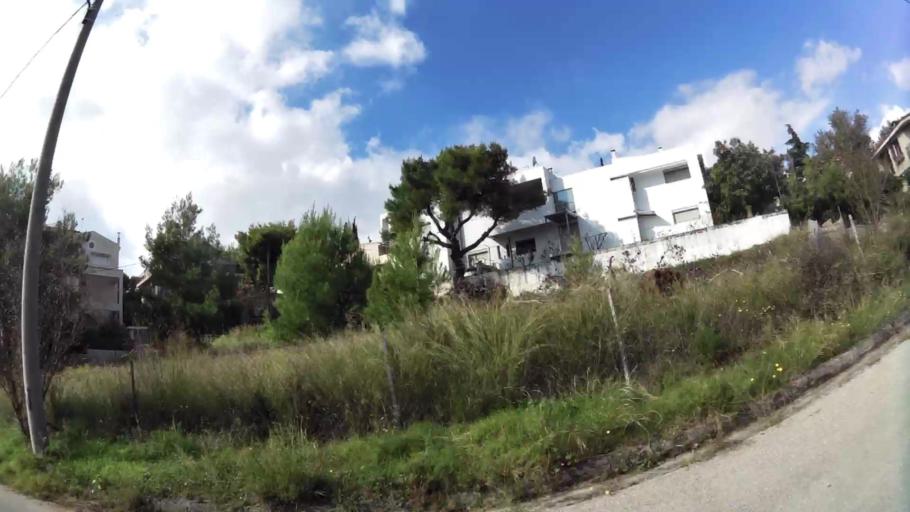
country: GR
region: Attica
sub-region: Nomarchia Athinas
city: Melissia
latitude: 38.0631
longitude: 23.8272
